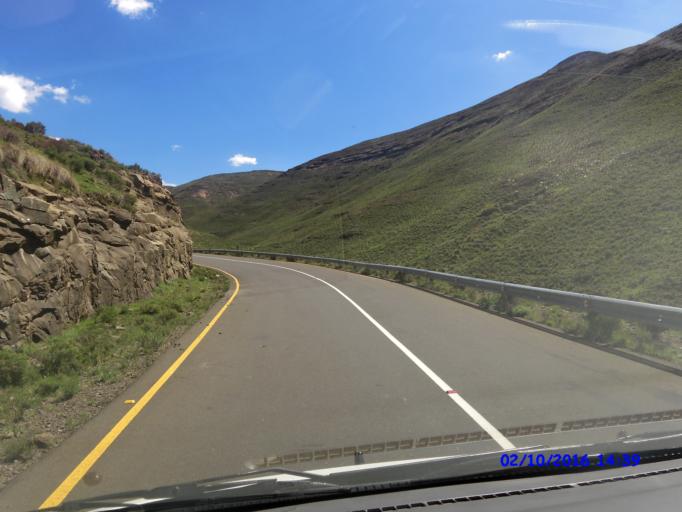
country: LS
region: Maseru
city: Nako
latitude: -29.5154
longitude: 28.0618
